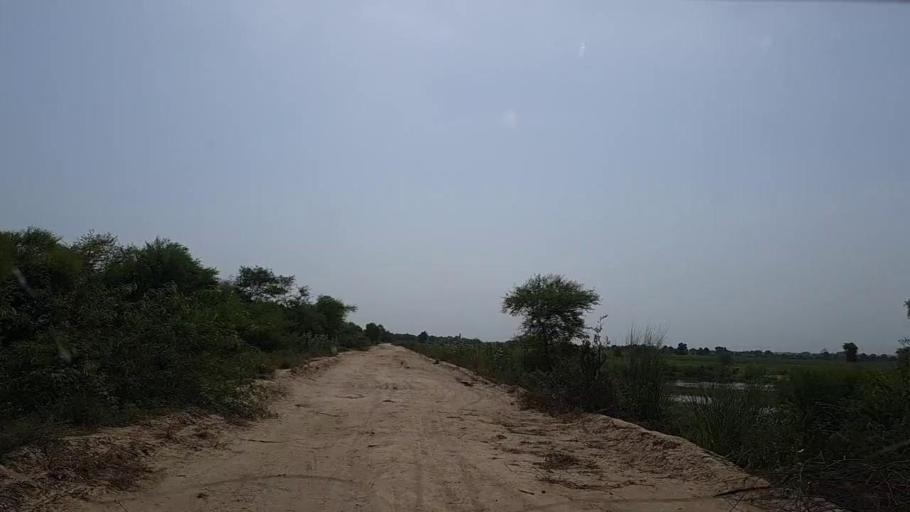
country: PK
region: Sindh
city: Ghotki
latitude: 28.0800
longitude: 69.3922
